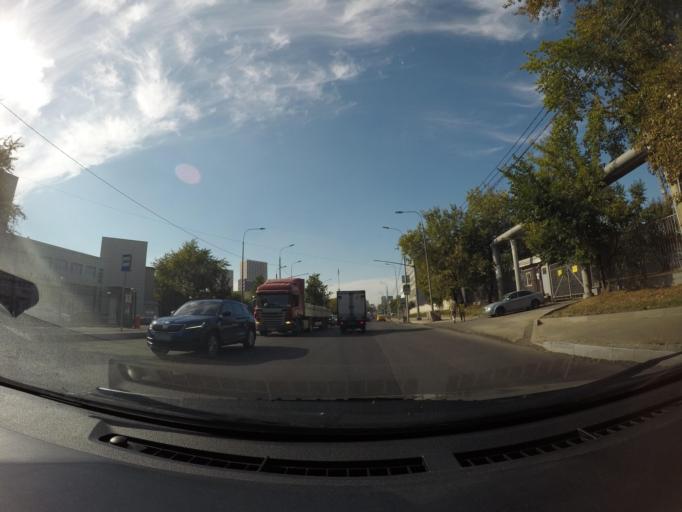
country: RU
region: Moscow
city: Mar'ina Roshcha
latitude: 55.8103
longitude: 37.6077
